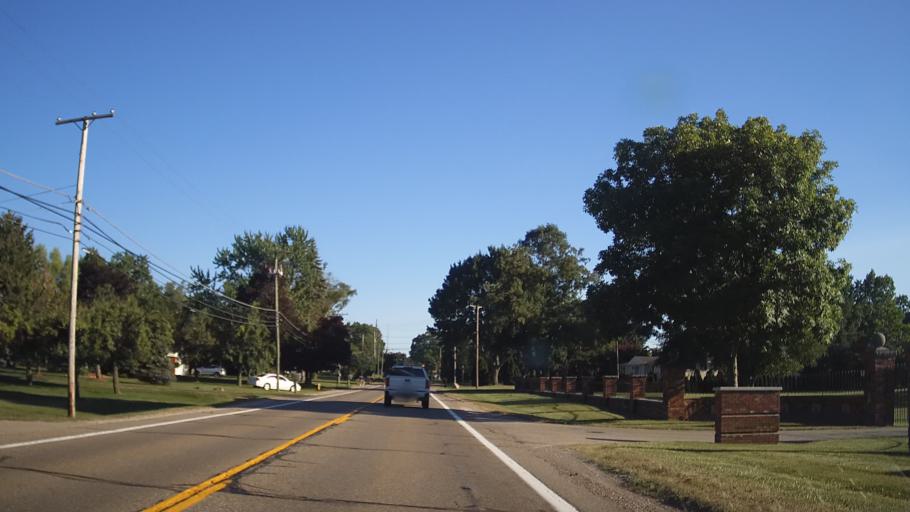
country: US
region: Michigan
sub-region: Macomb County
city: Clinton
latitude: 42.5922
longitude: -82.9137
